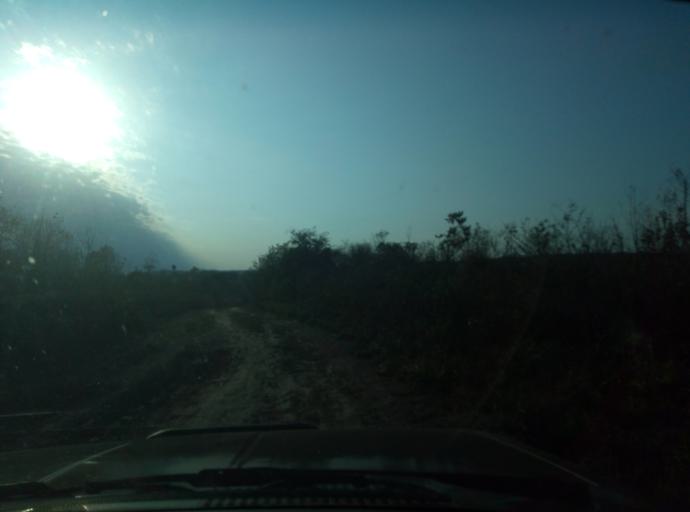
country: PY
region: Caaguazu
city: Doctor Cecilio Baez
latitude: -25.1989
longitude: -56.1220
